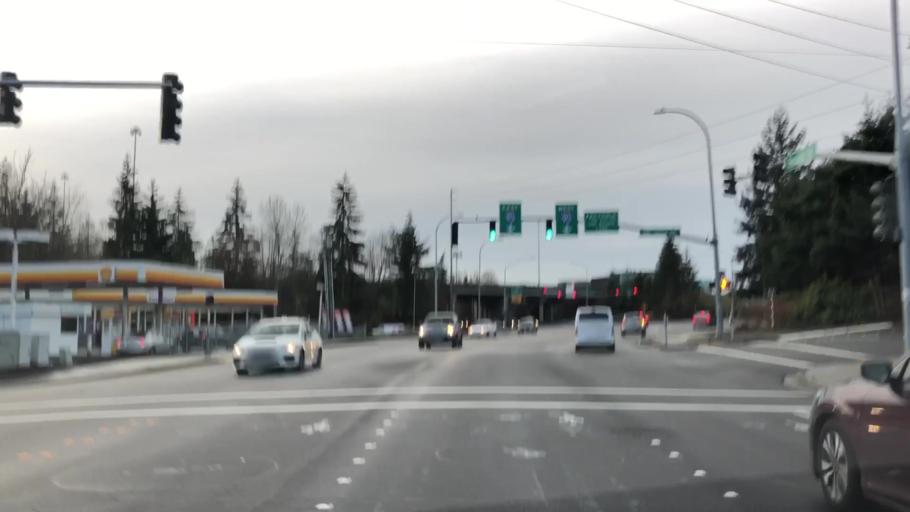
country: US
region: Washington
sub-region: King County
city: Newport
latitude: 47.5821
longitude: -122.1677
